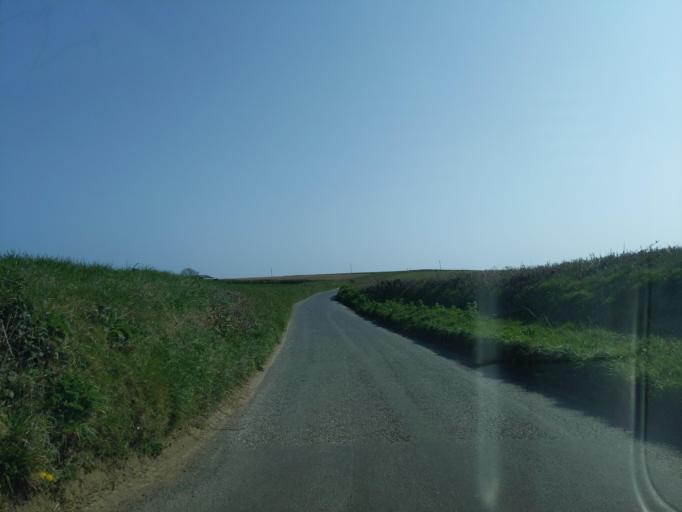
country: GB
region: England
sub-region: Devon
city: Dartmouth
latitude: 50.3450
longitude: -3.6559
